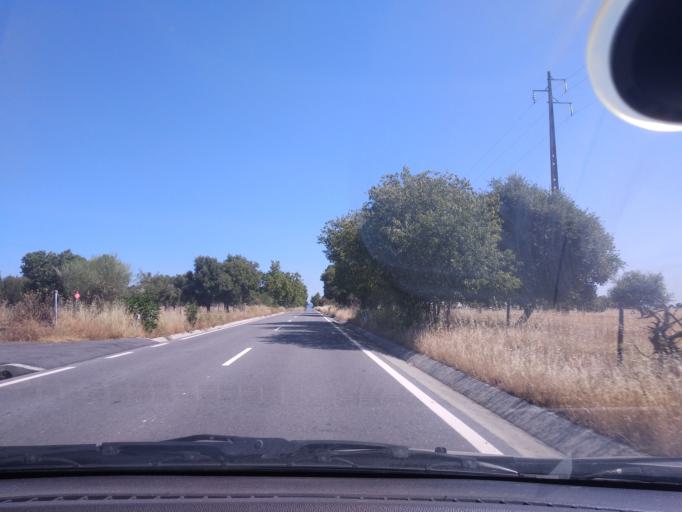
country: PT
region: Guarda
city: Alcains
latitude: 39.9423
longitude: -7.4568
